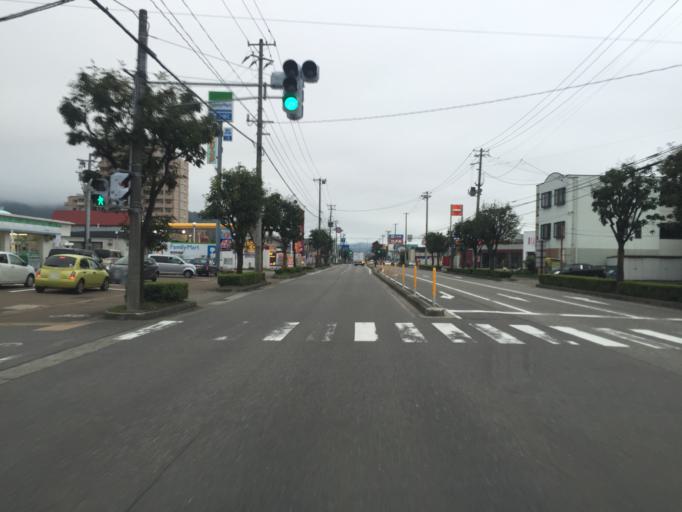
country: JP
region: Fukushima
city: Kitakata
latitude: 37.4964
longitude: 139.9428
